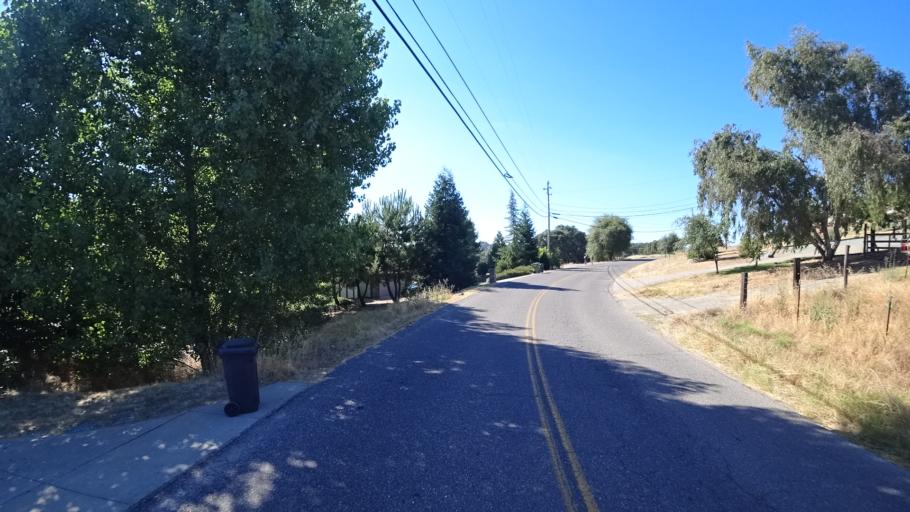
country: US
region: California
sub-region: Calaveras County
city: Rancho Calaveras
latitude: 38.1635
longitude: -120.8541
